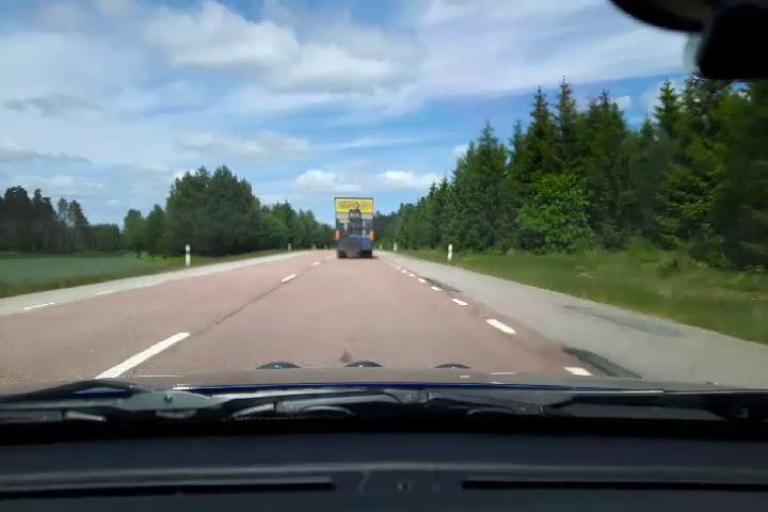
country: SE
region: Uppsala
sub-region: Osthammars Kommun
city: Bjorklinge
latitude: 60.1580
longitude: 17.4911
